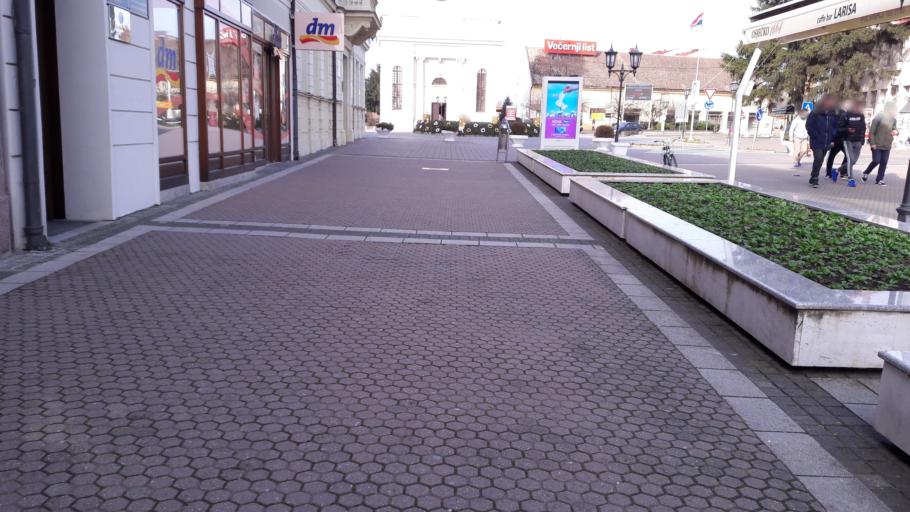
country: HR
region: Osjecko-Baranjska
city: Piskorevci
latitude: 45.3095
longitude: 18.4102
